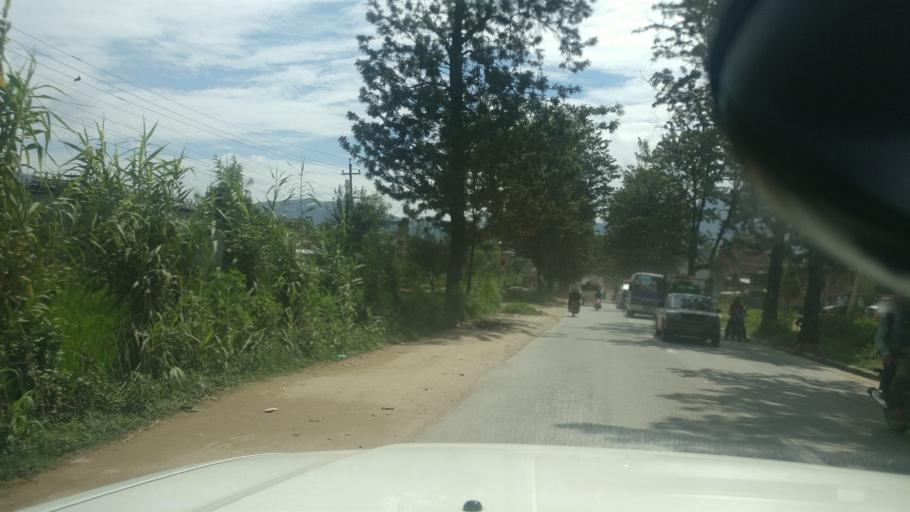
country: NP
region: Central Region
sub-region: Bagmati Zone
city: Bhaktapur
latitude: 27.6655
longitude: 85.4398
